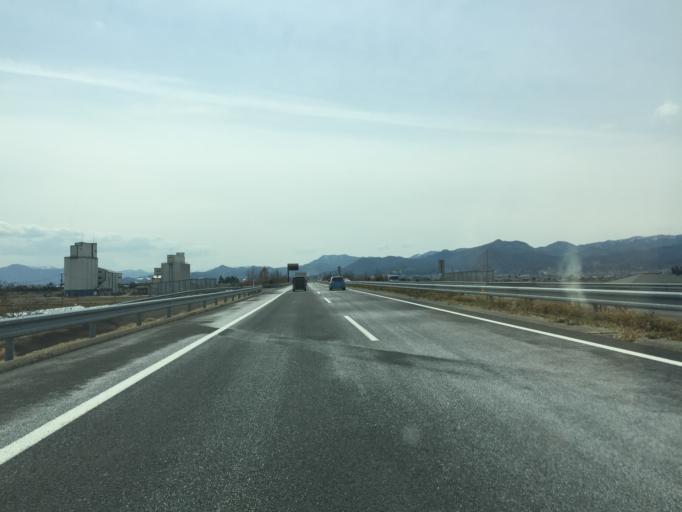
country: JP
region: Yamagata
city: Yamagata-shi
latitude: 38.2771
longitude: 140.2961
